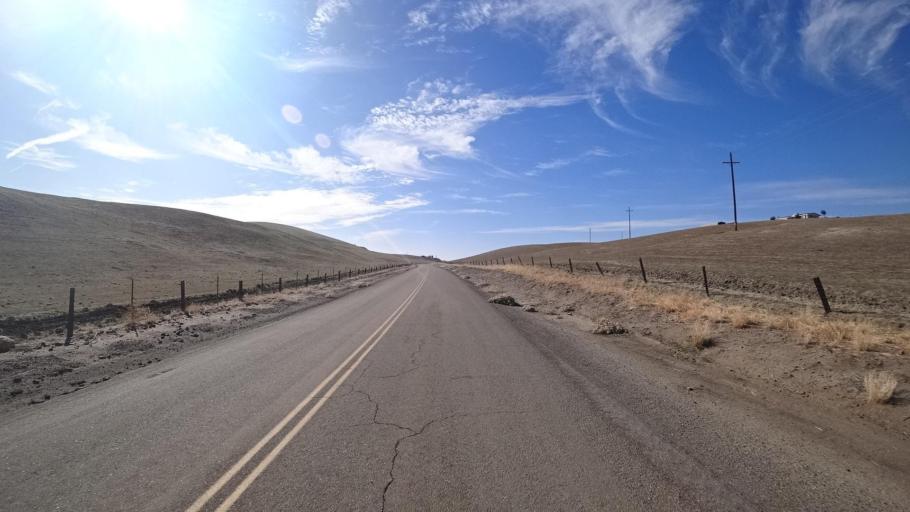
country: US
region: California
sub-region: Tulare County
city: Richgrove
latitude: 35.6364
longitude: -118.9489
